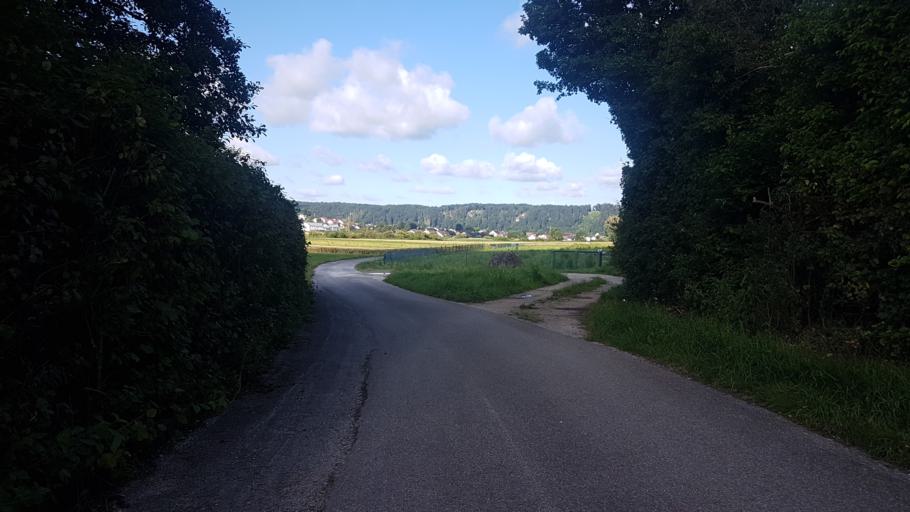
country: DE
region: Bavaria
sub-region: Upper Bavaria
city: Denkendorf
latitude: 48.9487
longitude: 11.3821
